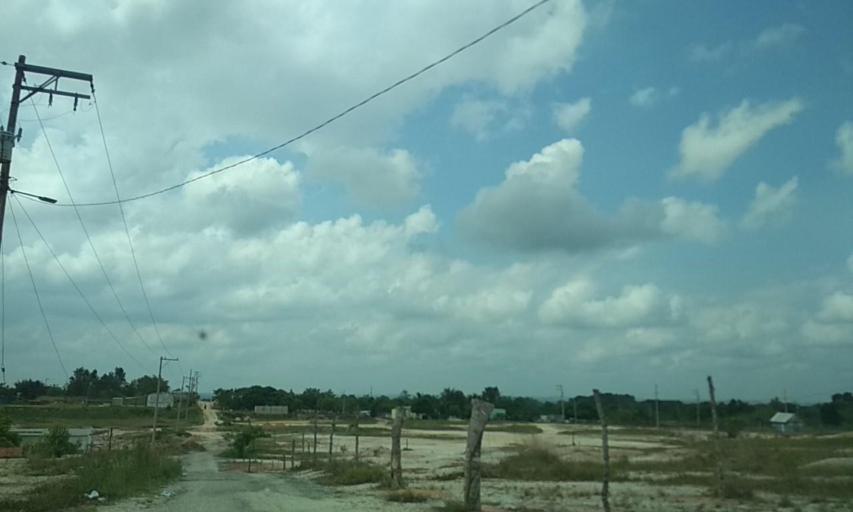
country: MX
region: Veracruz
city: Las Choapas
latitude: 17.9016
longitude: -94.1167
